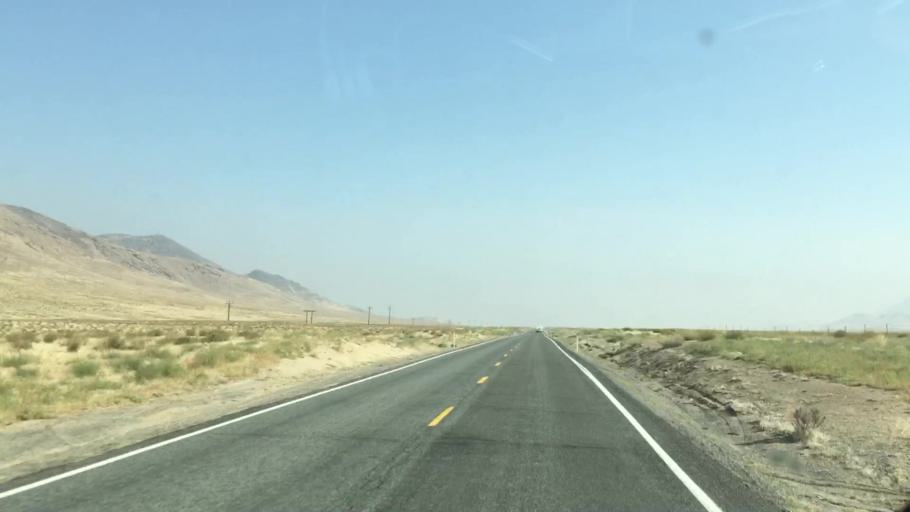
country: US
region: Nevada
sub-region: Lyon County
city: Fernley
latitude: 40.3947
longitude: -119.3336
